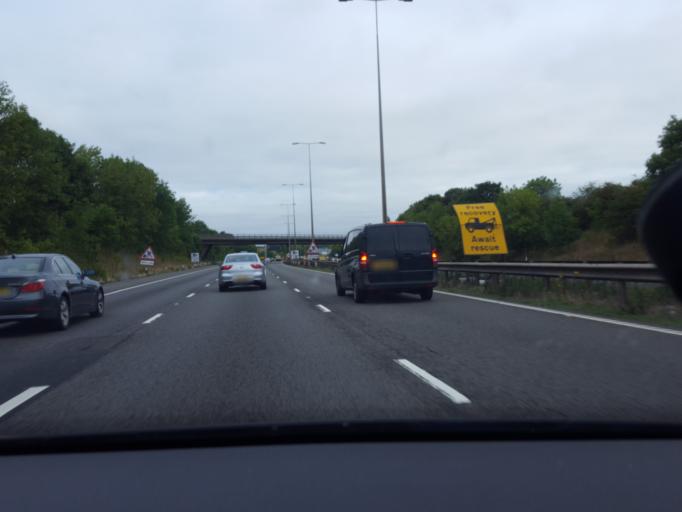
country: GB
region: England
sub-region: Leicestershire
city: Shepshed
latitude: 52.7991
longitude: -1.2987
